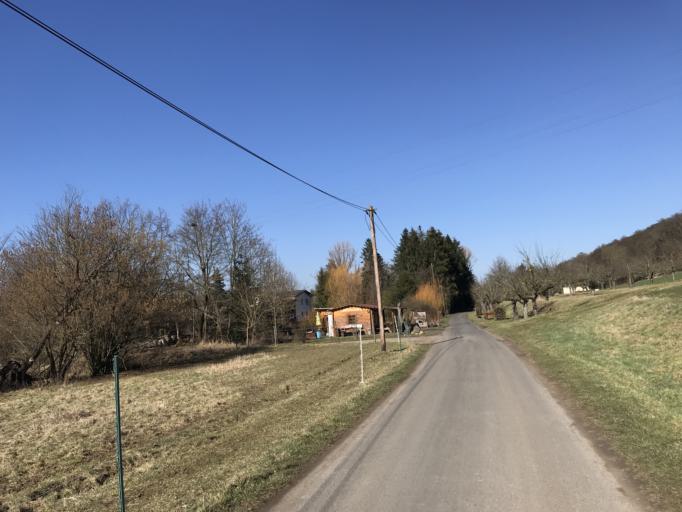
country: DE
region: Hesse
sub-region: Regierungsbezirk Darmstadt
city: Ranstadt
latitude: 50.3653
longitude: 8.9807
